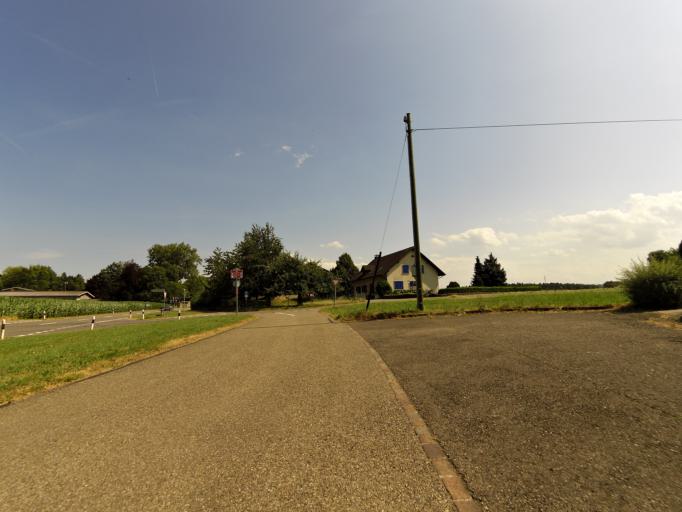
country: CH
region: Aargau
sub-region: Bezirk Baden
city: Birmenstorf
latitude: 47.4564
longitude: 8.2616
